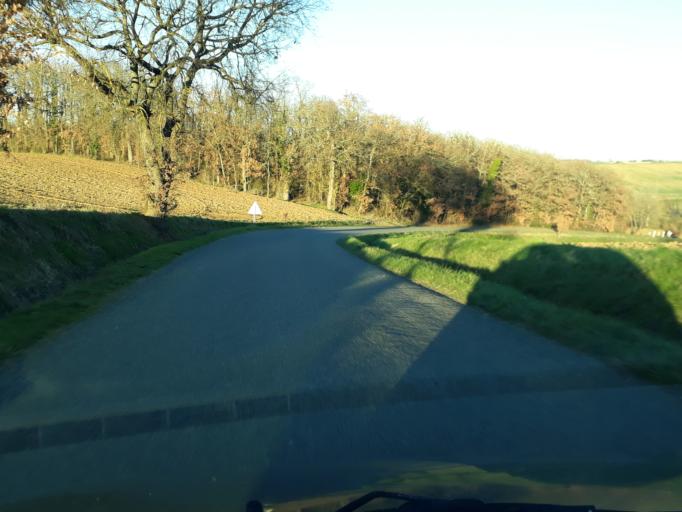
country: FR
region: Midi-Pyrenees
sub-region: Departement du Gers
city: Gimont
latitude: 43.6245
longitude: 0.9188
